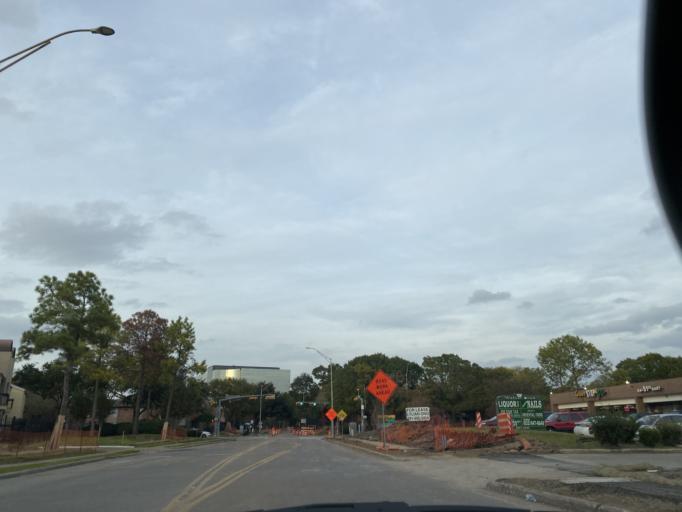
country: US
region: Texas
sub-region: Harris County
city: Bunker Hill Village
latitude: 29.7317
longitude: -95.5678
